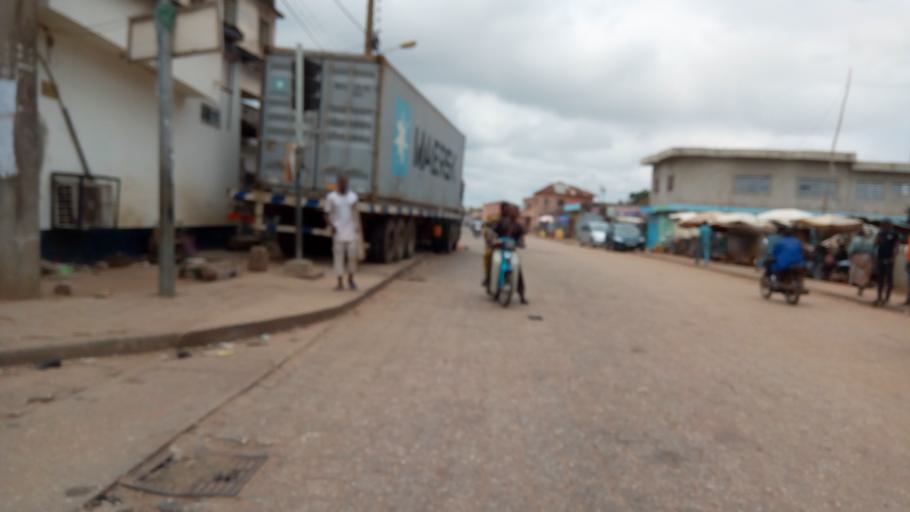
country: BJ
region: Queme
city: Porto-Novo
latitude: 6.4826
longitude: 2.6297
